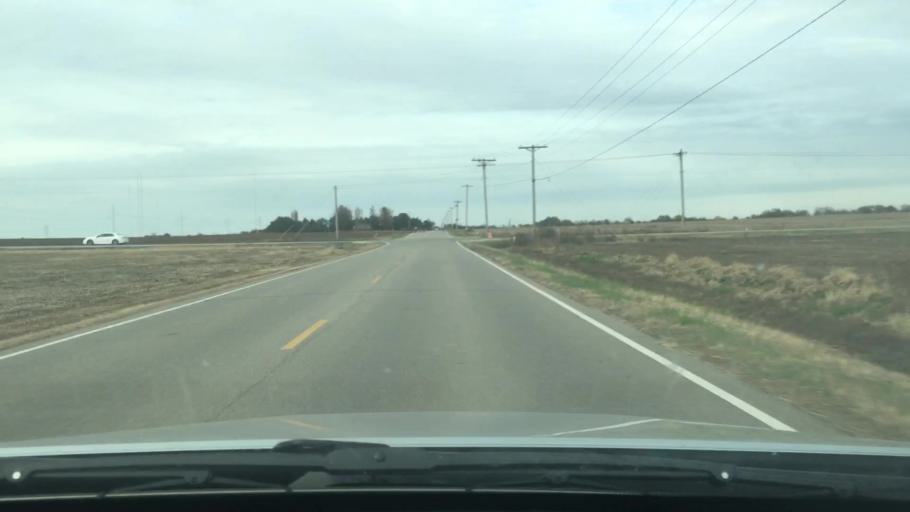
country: US
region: Kansas
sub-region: Sedgwick County
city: Maize
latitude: 37.7358
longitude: -97.4991
